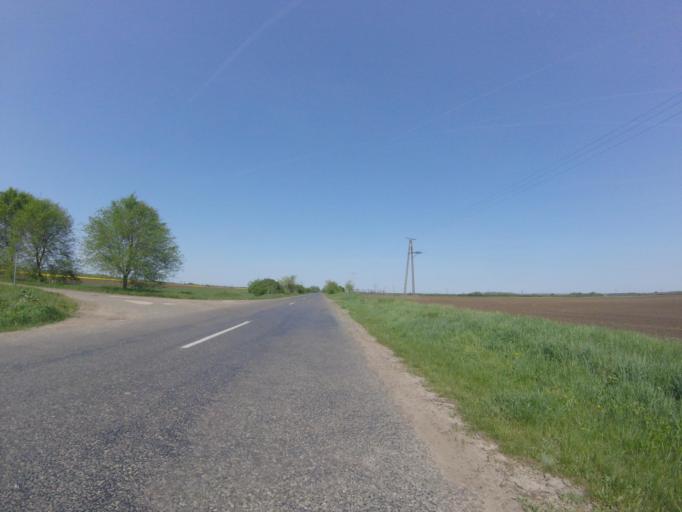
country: HU
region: Pest
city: Nyaregyhaza
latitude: 47.2401
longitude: 19.5201
